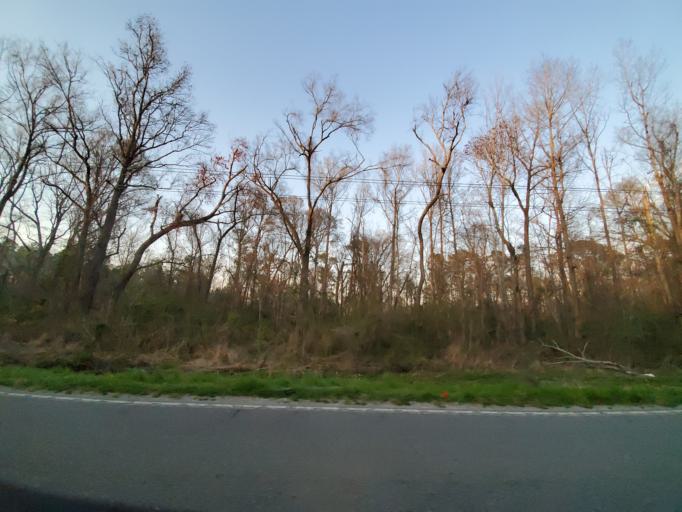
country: US
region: South Carolina
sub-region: Dorchester County
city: Ridgeville
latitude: 33.0188
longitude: -80.3520
